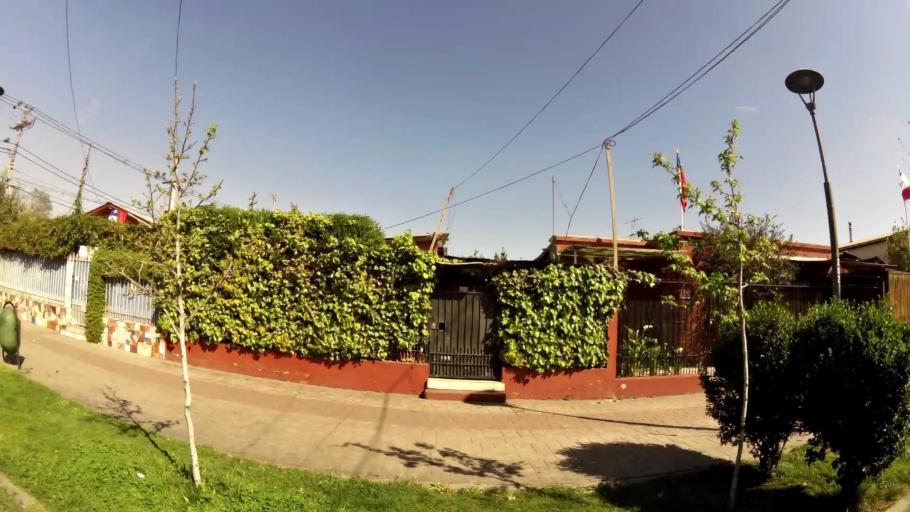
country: CL
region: Santiago Metropolitan
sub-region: Provincia de Santiago
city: La Pintana
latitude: -33.5312
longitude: -70.6103
